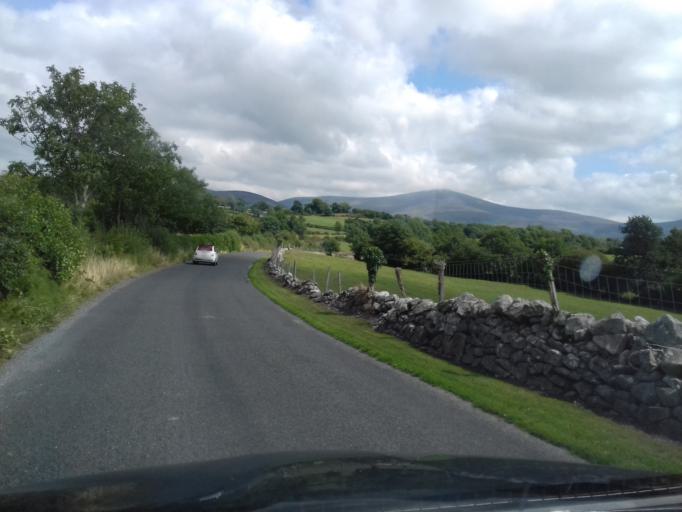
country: IE
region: Leinster
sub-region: Kilkenny
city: Graiguenamanagh
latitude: 52.6091
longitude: -6.9002
